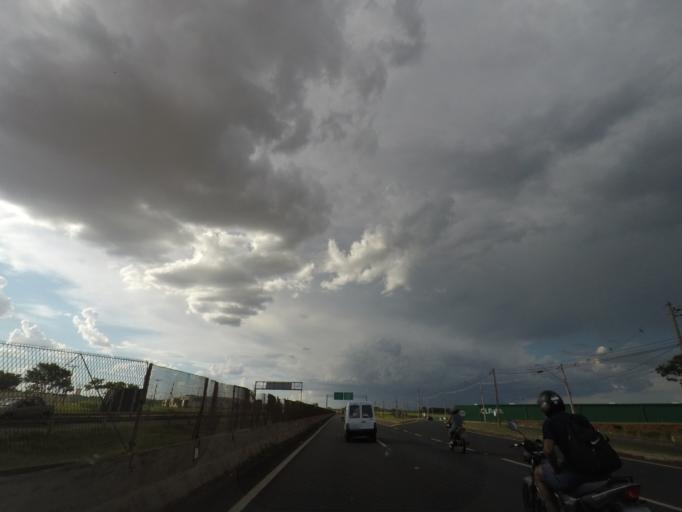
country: BR
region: Sao Paulo
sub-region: Ribeirao Preto
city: Ribeirao Preto
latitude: -21.1226
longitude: -47.7730
